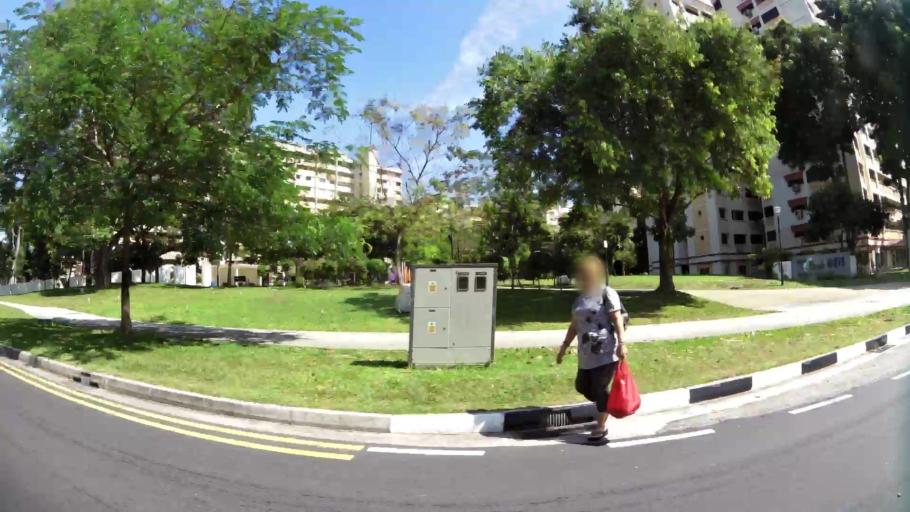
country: SG
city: Singapore
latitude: 1.3774
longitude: 103.8374
